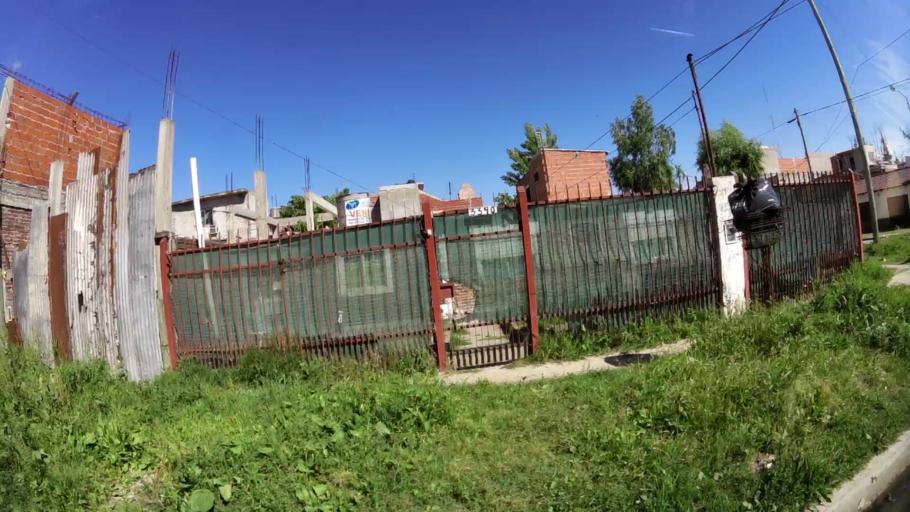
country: AR
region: Buenos Aires
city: Caseros
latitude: -34.5319
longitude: -58.5889
